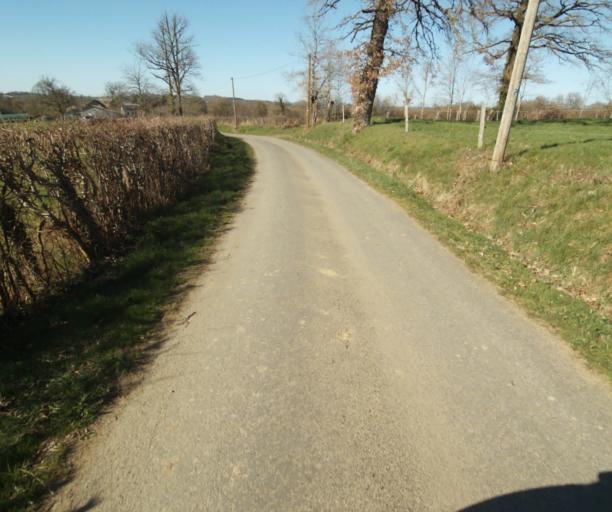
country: FR
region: Limousin
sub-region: Departement de la Correze
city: Chamboulive
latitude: 45.4296
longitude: 1.6512
